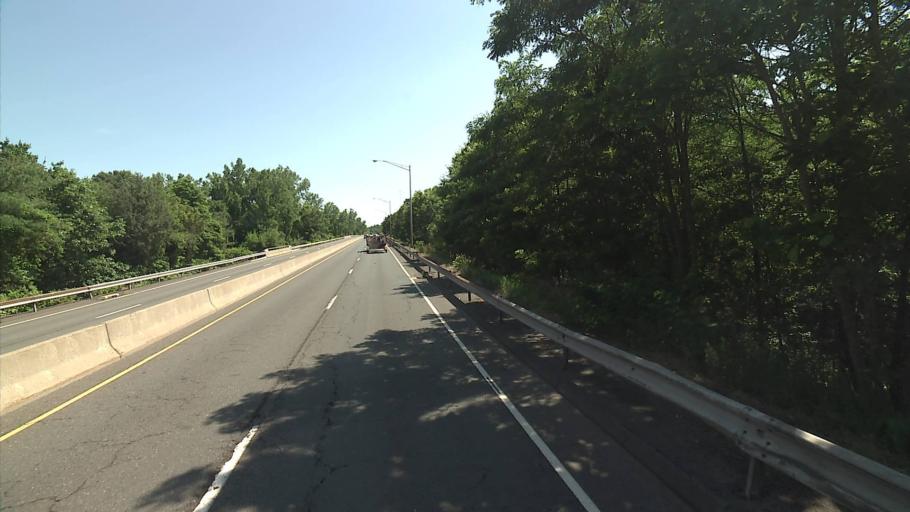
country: US
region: Connecticut
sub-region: Hartford County
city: Plainville
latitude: 41.6749
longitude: -72.8815
